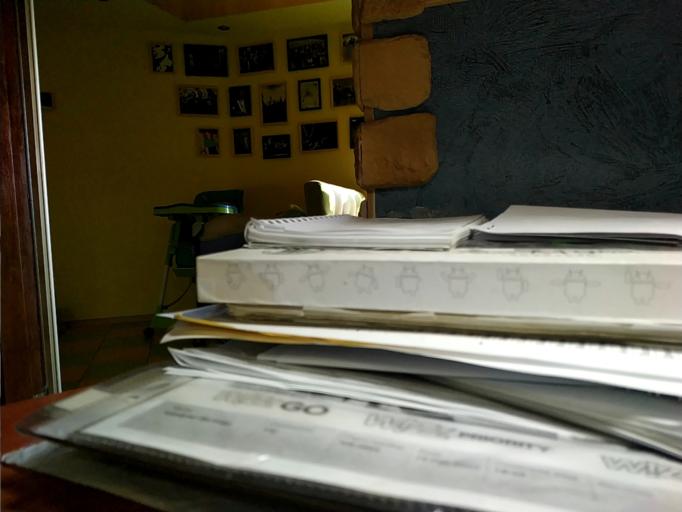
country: RU
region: Novgorod
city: Kholm
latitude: 57.1566
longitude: 31.4240
